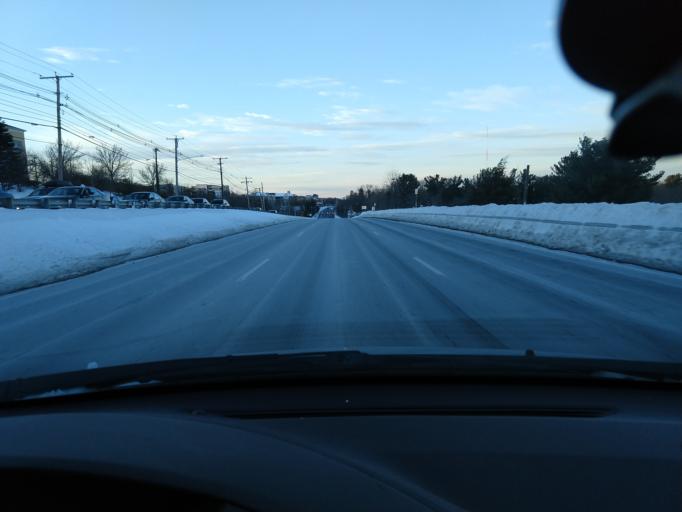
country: US
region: Massachusetts
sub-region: Middlesex County
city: Burlington
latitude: 42.4821
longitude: -71.2180
